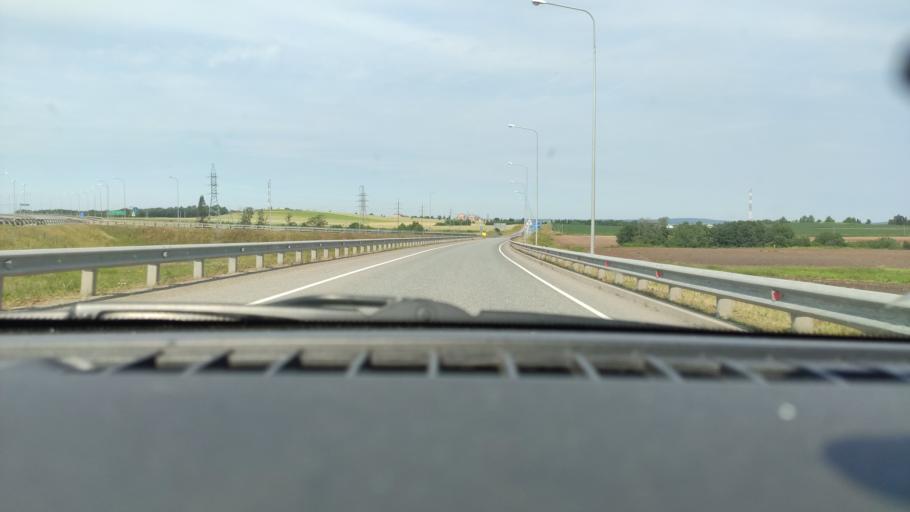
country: RU
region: Perm
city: Lobanovo
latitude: 57.8484
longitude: 56.2964
